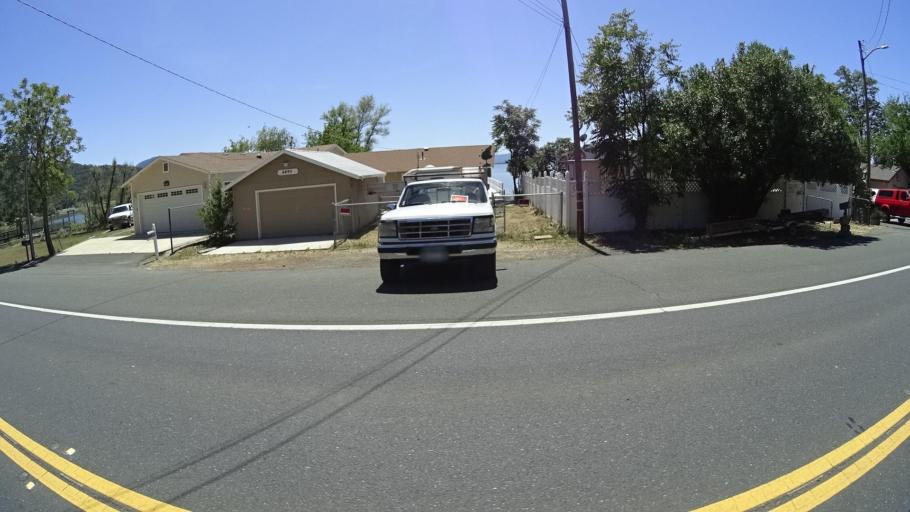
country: US
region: California
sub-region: Lake County
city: Lucerne
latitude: 39.0789
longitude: -122.7860
